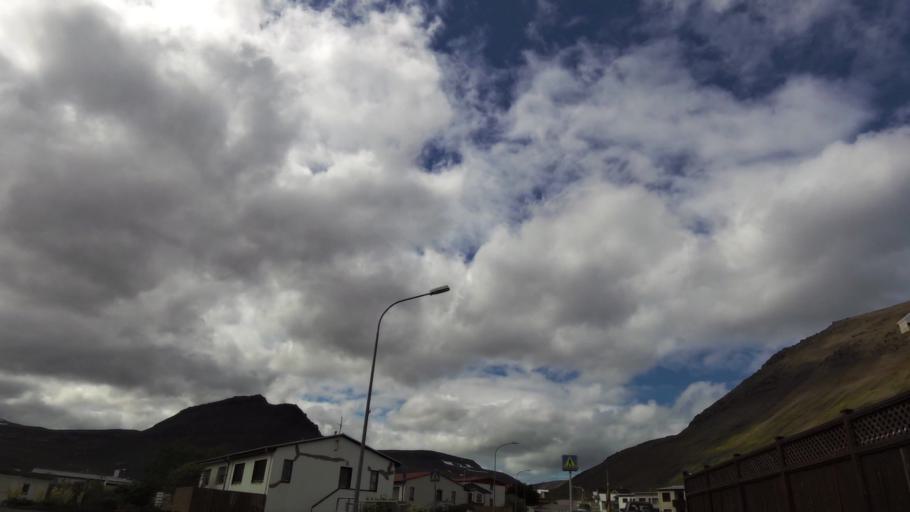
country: IS
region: Westfjords
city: Isafjoerdur
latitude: 66.1570
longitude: -23.2519
